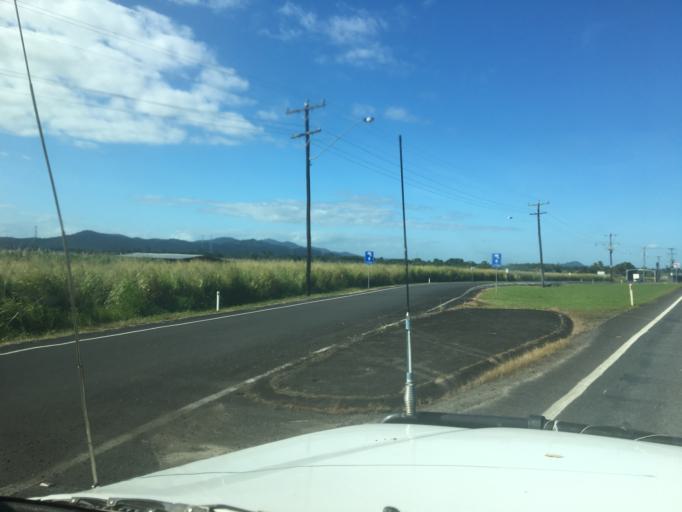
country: AU
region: Queensland
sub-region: Cassowary Coast
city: Innisfail
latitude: -17.3192
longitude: 145.9278
